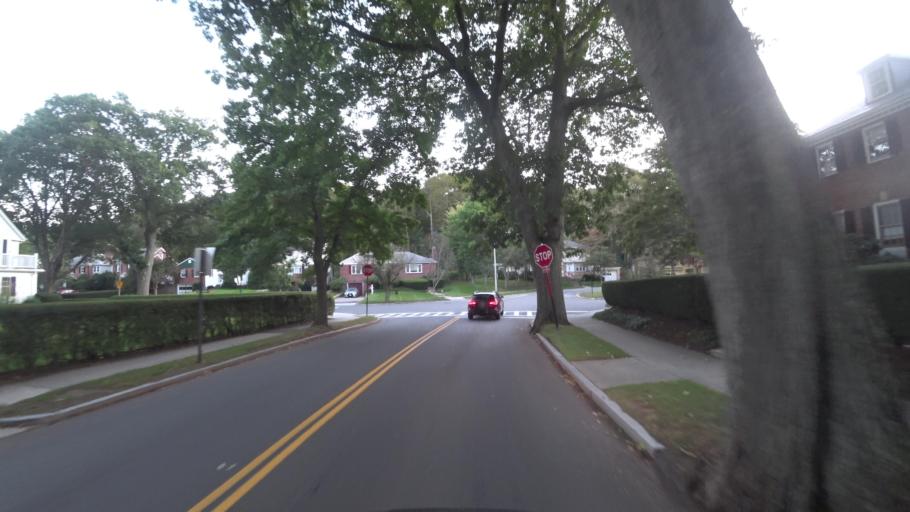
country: US
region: Massachusetts
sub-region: Norfolk County
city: Brookline
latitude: 42.3296
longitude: -71.1500
